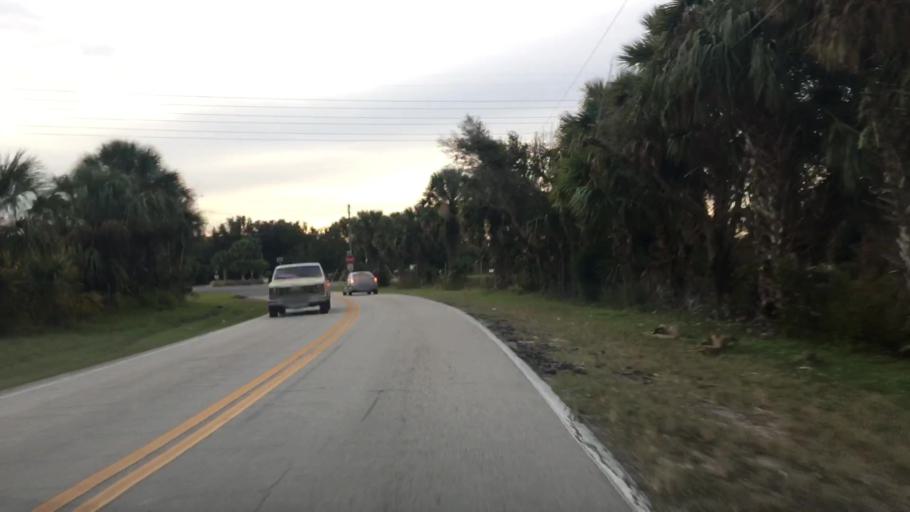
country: US
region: Florida
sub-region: Seminole County
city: Midway
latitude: 28.8216
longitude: -81.1856
